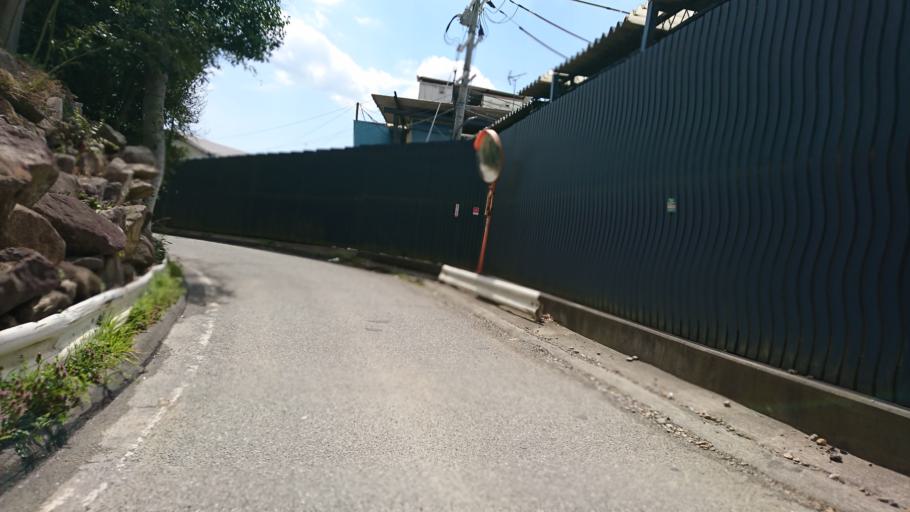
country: JP
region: Hyogo
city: Miki
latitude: 34.7708
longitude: 134.9610
